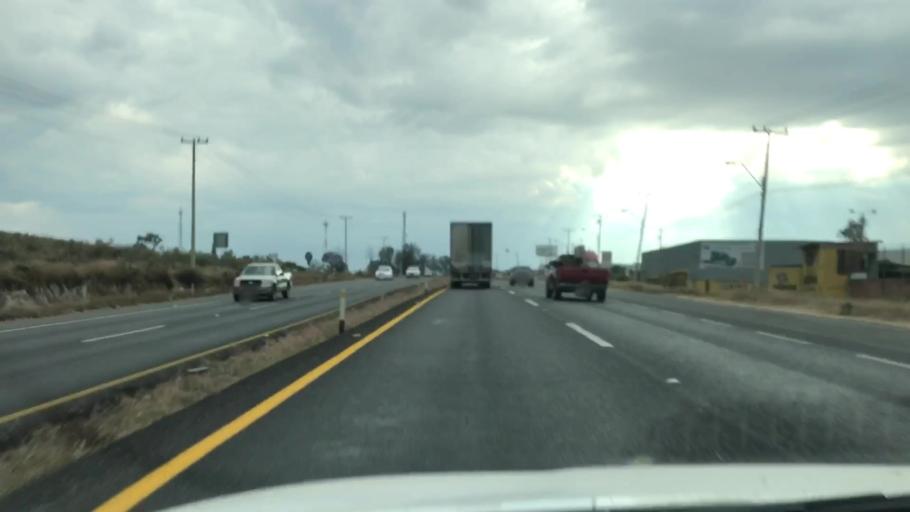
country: MX
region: Guanajuato
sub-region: Irapuato
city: San Ignacio de Rivera (Ojo de Agua)
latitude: 20.5697
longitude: -101.4445
